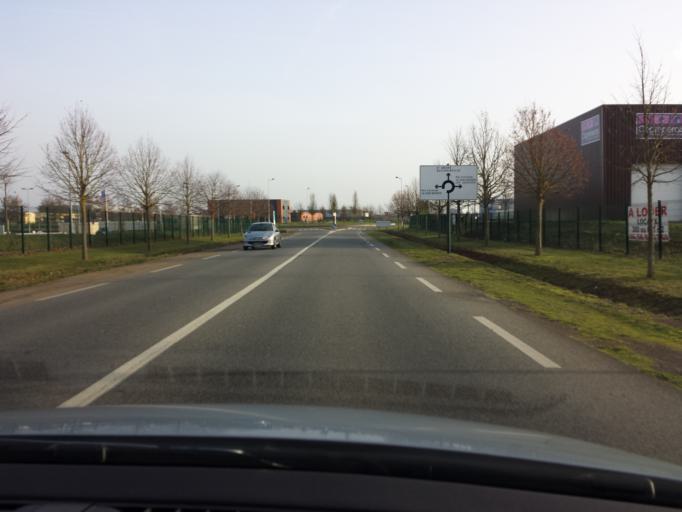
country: FR
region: Haute-Normandie
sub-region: Departement de l'Eure
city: Evreux
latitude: 49.0045
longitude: 1.1751
